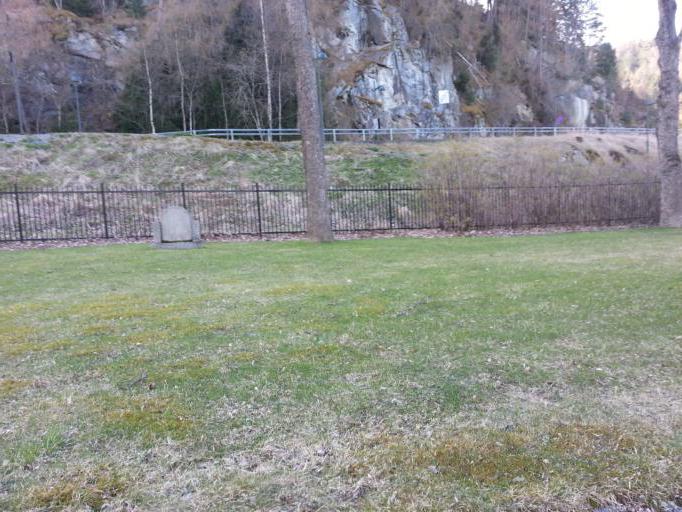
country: NO
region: Sor-Trondelag
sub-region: Trondheim
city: Trondheim
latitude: 63.4306
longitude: 10.3570
